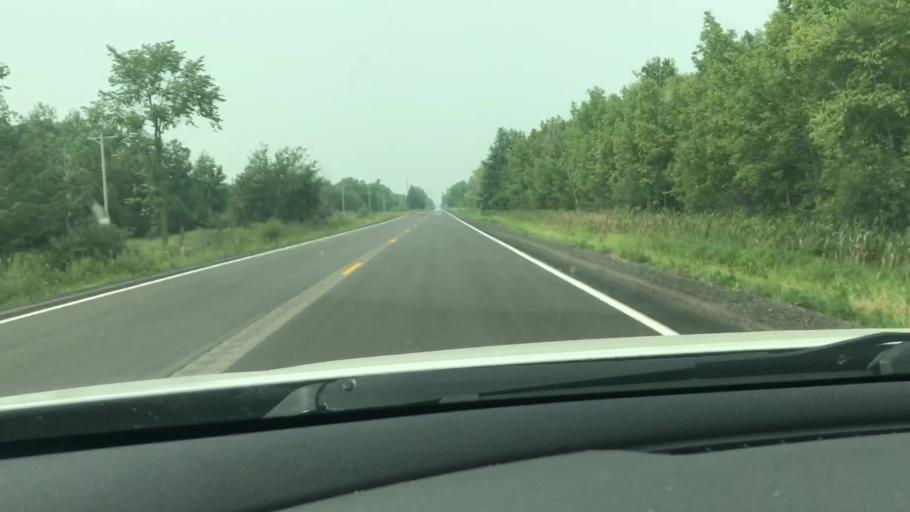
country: US
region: Minnesota
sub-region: Itasca County
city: Cohasset
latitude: 47.3629
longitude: -93.8688
